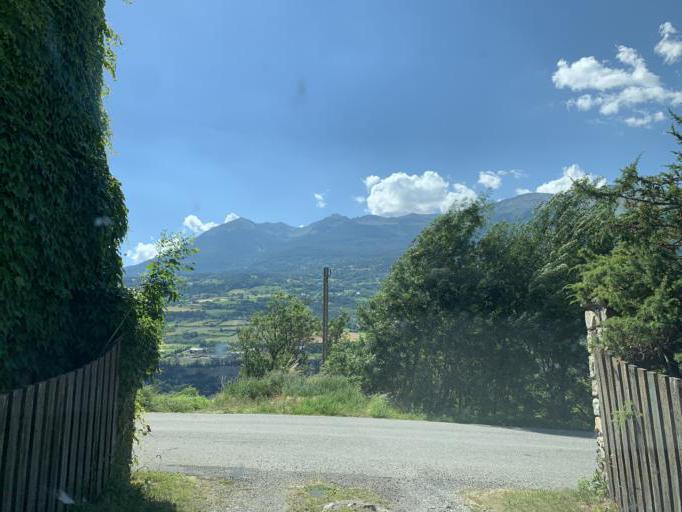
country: FR
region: Provence-Alpes-Cote d'Azur
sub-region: Departement des Hautes-Alpes
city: Embrun
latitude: 44.5826
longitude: 6.5288
